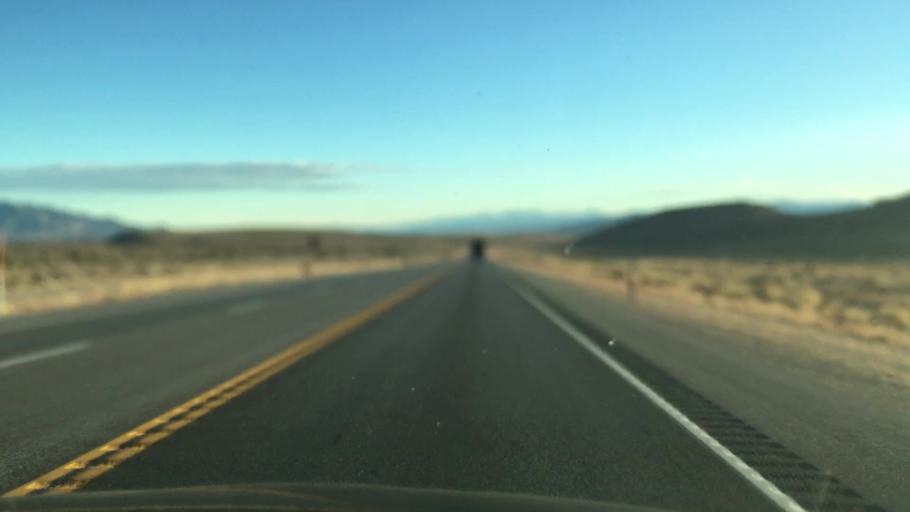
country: US
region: Nevada
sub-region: Esmeralda County
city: Goldfield
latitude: 37.6629
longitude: -117.2179
